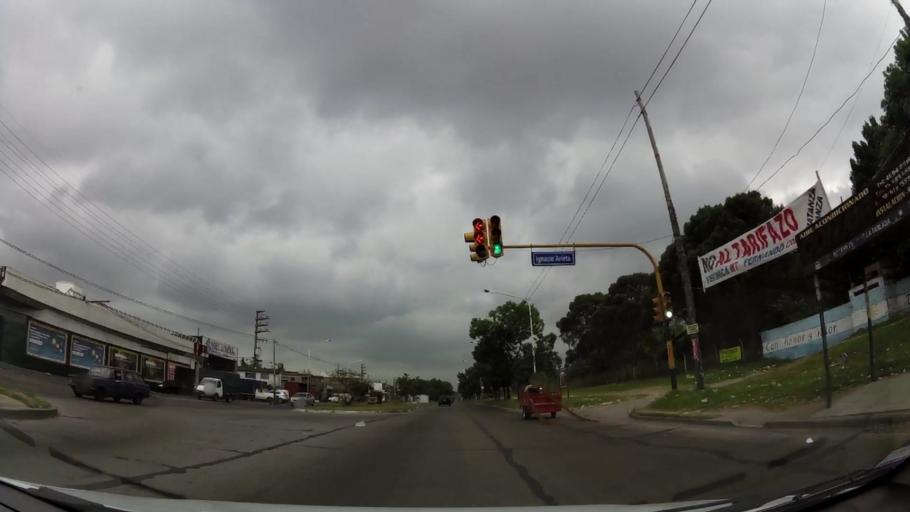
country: AR
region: Buenos Aires
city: San Justo
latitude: -34.6970
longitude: -58.5364
